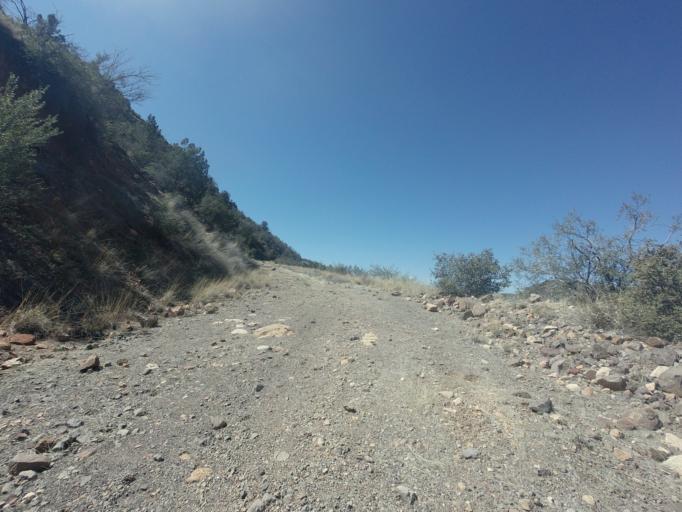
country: US
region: Arizona
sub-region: Gila County
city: Pine
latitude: 34.4048
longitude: -111.6066
